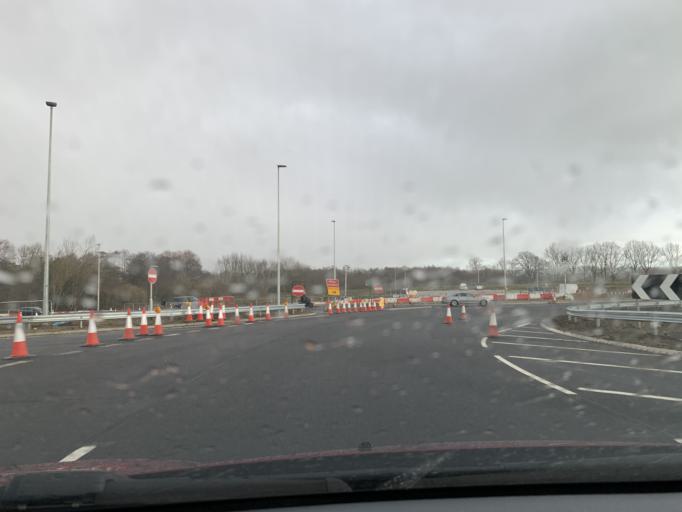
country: GB
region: England
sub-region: Kent
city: Ashford
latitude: 51.1334
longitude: 0.9205
